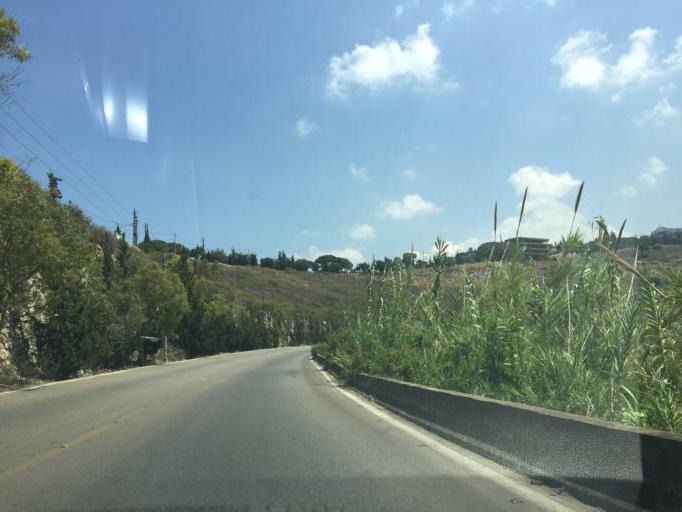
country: LB
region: Mont-Liban
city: Beit ed Dine
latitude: 33.7076
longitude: 35.4529
